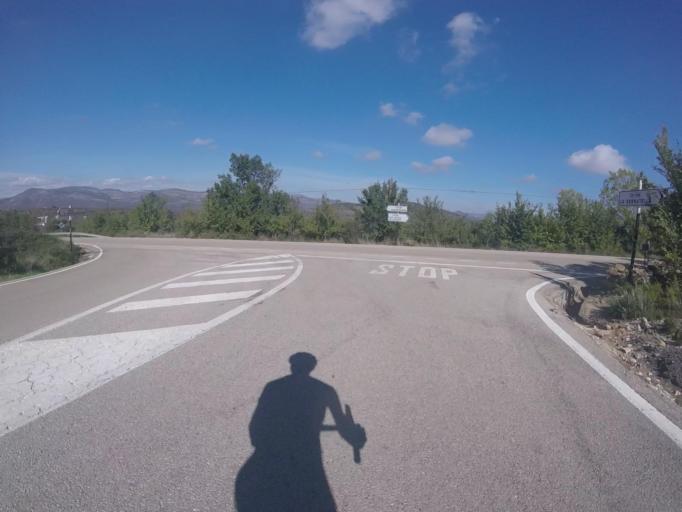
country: ES
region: Valencia
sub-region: Provincia de Castello
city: Albocasser
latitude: 40.3573
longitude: 0.0377
